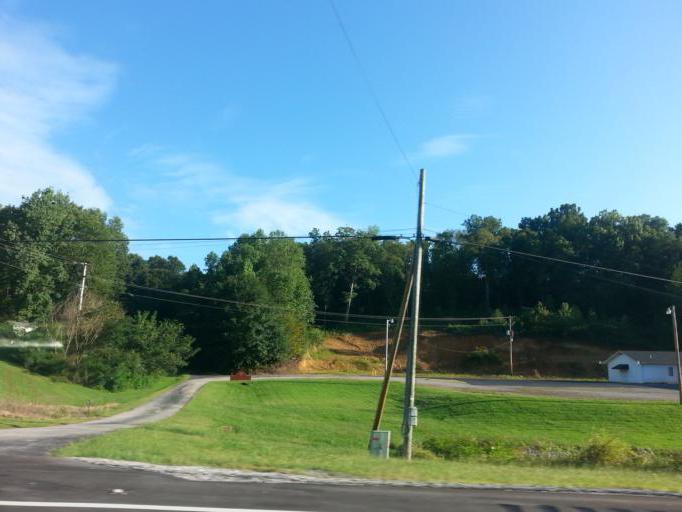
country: US
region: Alabama
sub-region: Lauderdale County
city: Killen
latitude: 34.8597
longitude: -87.5125
